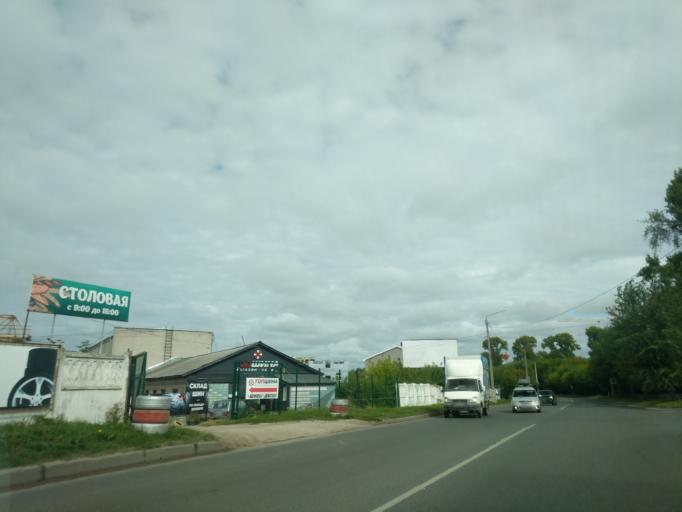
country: RU
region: Kirov
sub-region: Kirovo-Chepetskiy Rayon
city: Kirov
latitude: 58.5995
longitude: 49.6433
